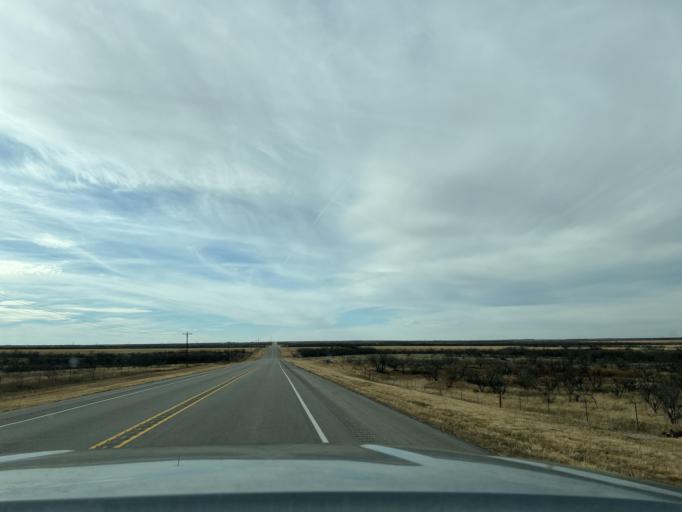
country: US
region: Texas
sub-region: Jones County
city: Anson
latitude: 32.7506
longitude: -99.6814
